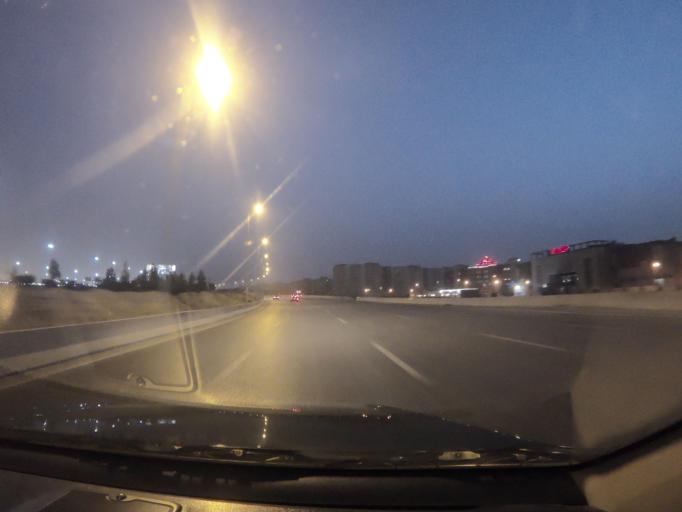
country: EG
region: Muhafazat al Qahirah
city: Cairo
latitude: 30.0473
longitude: 31.4051
